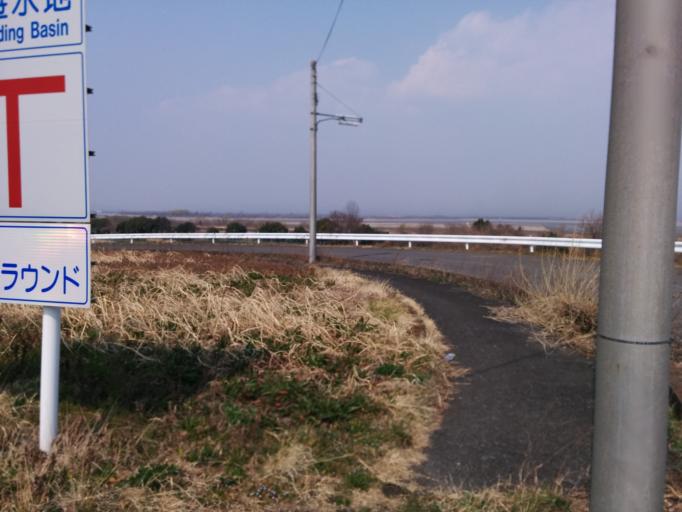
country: JP
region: Ibaraki
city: Koga
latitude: 36.2011
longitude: 139.6761
